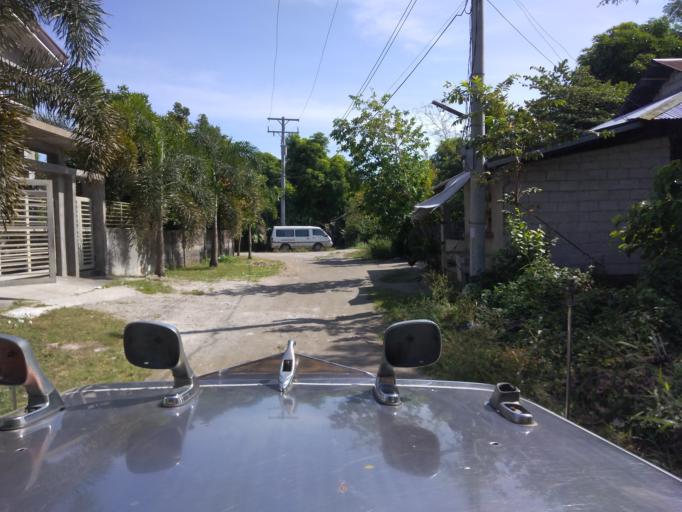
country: PH
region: Central Luzon
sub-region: Province of Pampanga
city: Bacolor
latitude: 15.0039
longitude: 120.6708
